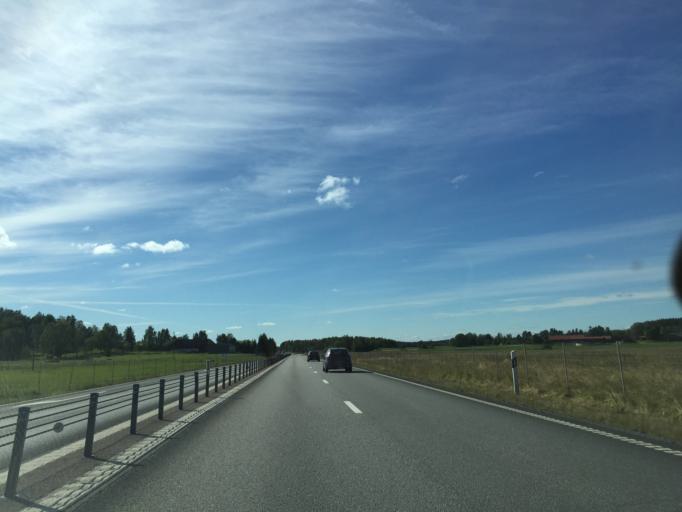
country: SE
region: Vaestmanland
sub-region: Kopings Kommun
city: Koping
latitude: 59.5696
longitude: 16.0891
